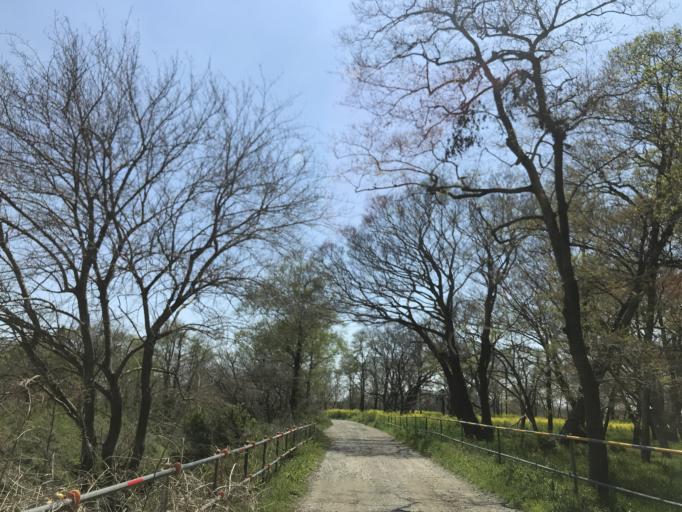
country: JP
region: Ibaraki
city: Moriya
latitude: 35.9218
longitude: 139.9921
